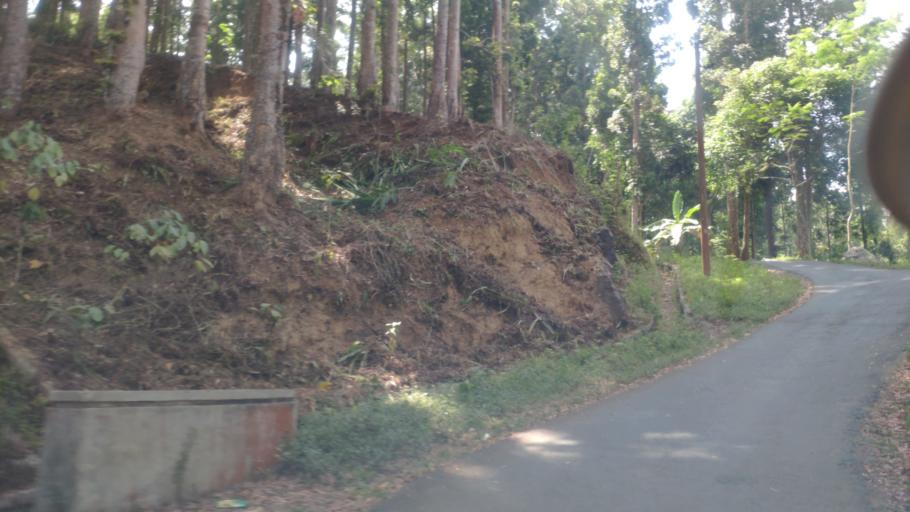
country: ID
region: Central Java
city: Wonosobo
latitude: -7.4513
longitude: 109.7205
